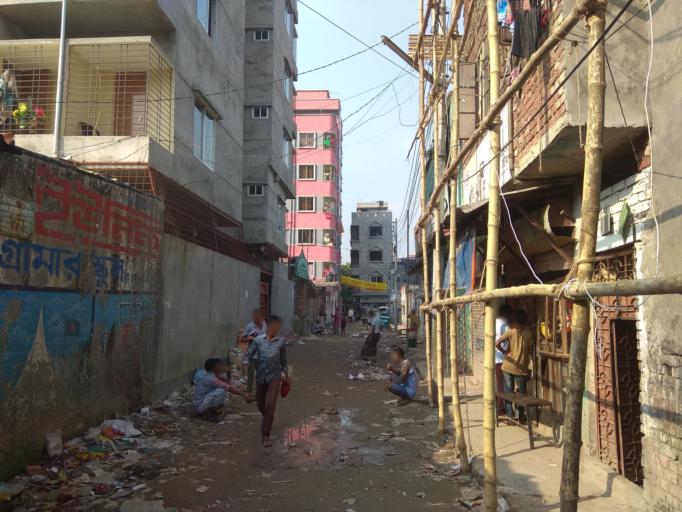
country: BD
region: Dhaka
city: Tungi
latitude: 23.8178
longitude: 90.3707
